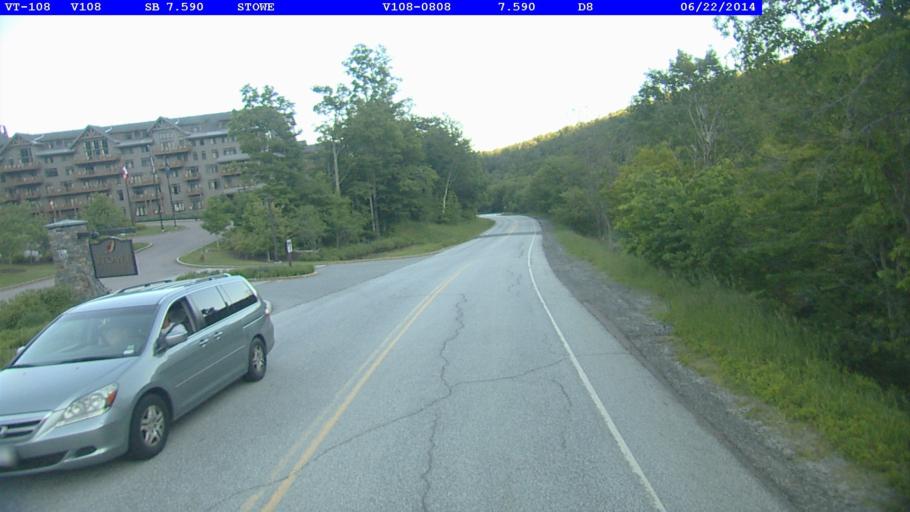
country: US
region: Vermont
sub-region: Lamoille County
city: Johnson
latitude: 44.5304
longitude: -72.7832
